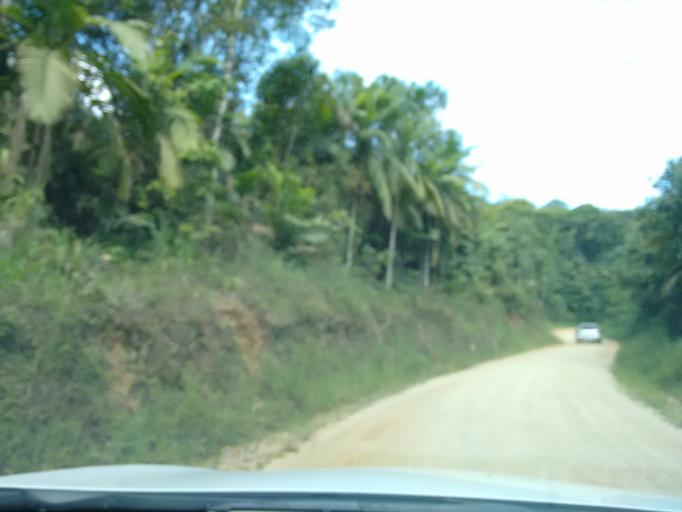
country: BR
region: Santa Catarina
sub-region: Pomerode
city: Pomerode
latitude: -26.7089
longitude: -49.0942
